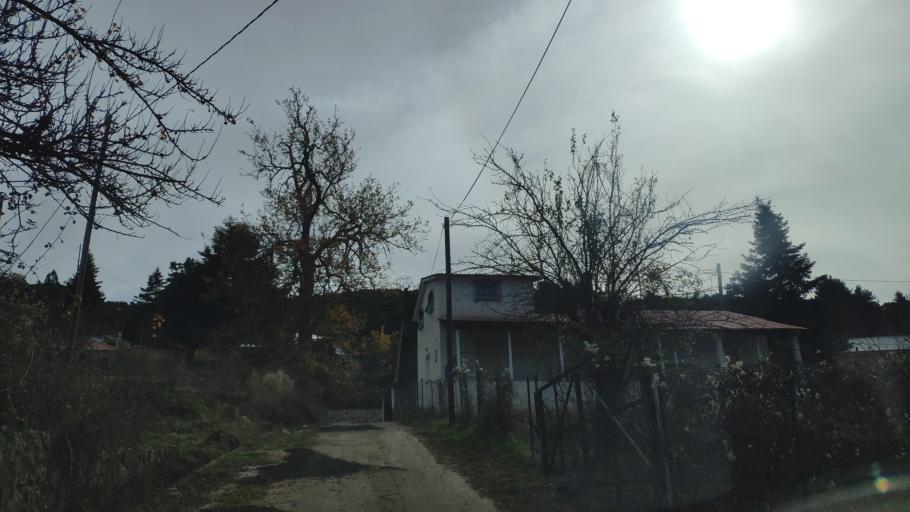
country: GR
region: West Greece
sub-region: Nomos Achaias
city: Aiyira
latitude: 38.0305
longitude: 22.3678
